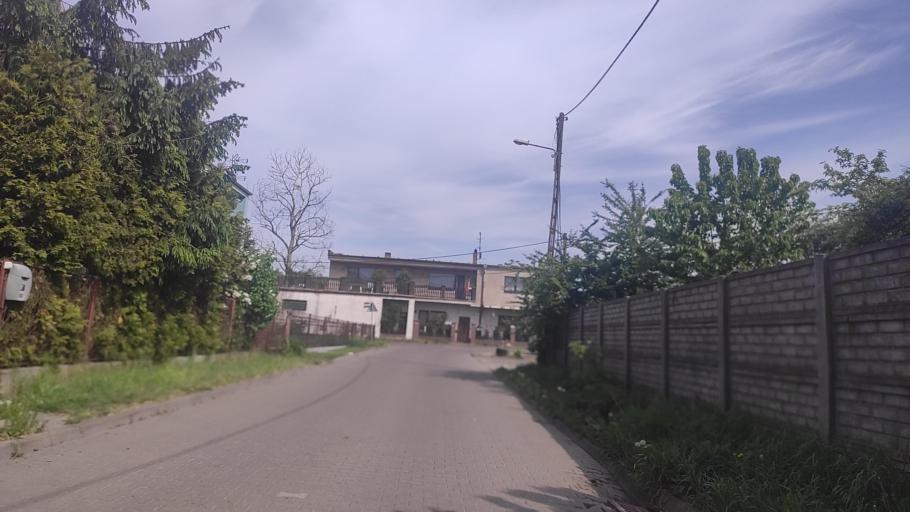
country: PL
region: Greater Poland Voivodeship
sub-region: Powiat poznanski
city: Swarzedz
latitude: 52.4071
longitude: 17.0915
